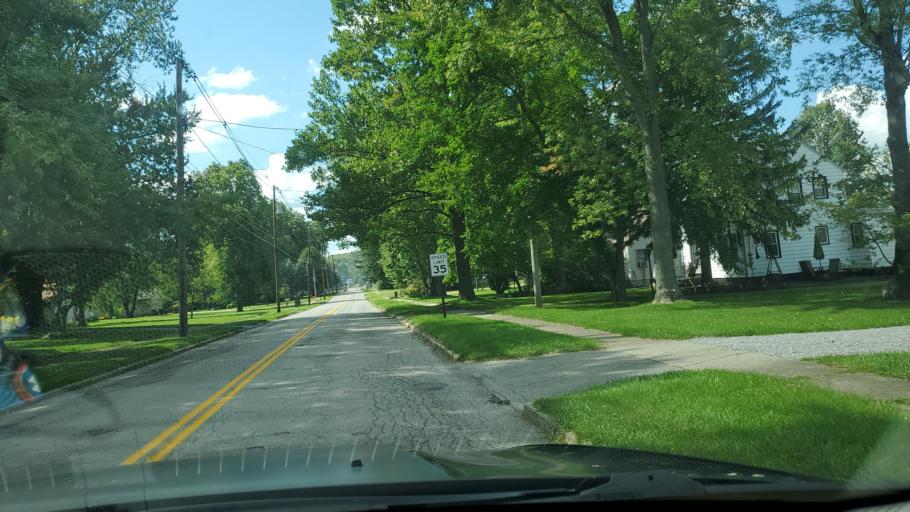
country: US
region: Ohio
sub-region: Mahoning County
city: Boardman
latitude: 41.0165
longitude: -80.6568
